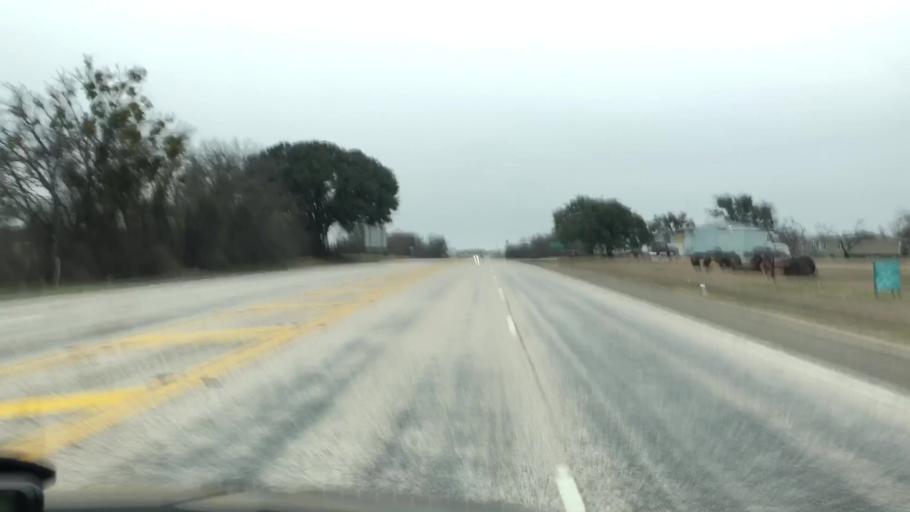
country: US
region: Texas
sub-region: Hamilton County
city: Hamilton
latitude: 31.4829
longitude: -98.1501
